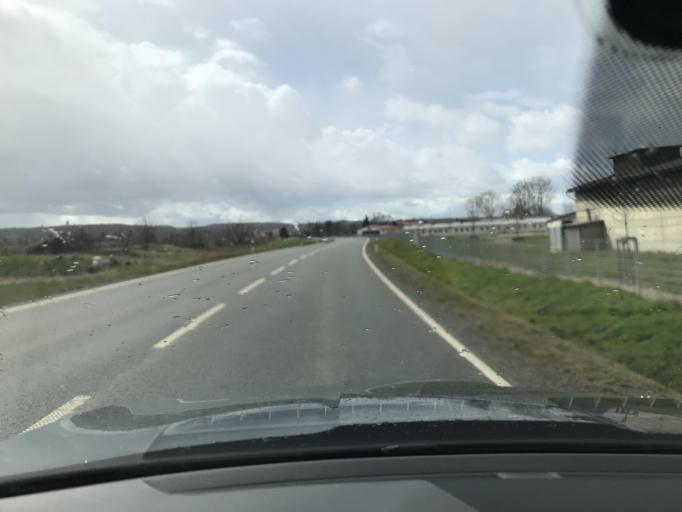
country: DE
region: Saxony-Anhalt
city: Ballenstedt
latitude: 51.7293
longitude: 11.2568
